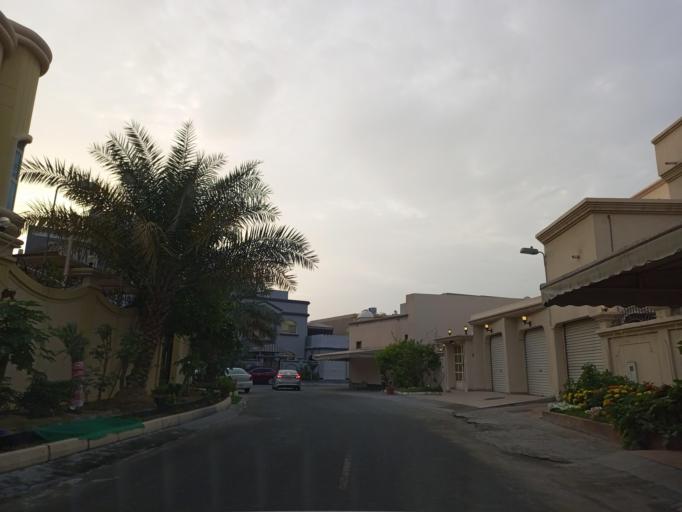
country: BH
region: Muharraq
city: Al Hadd
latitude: 26.2466
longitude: 50.6445
